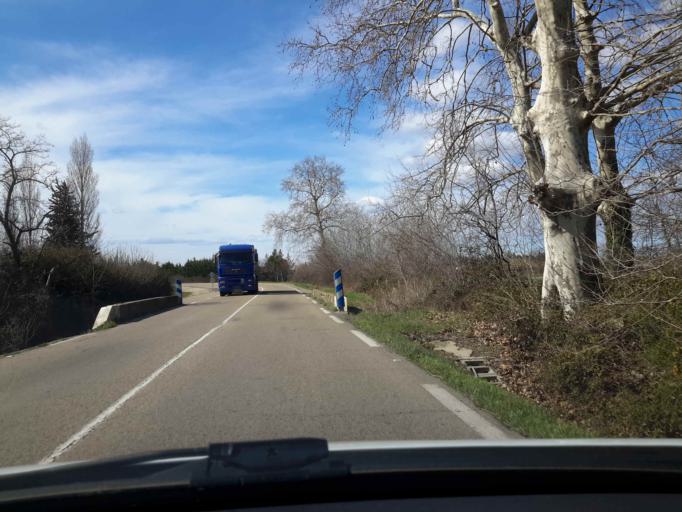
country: FR
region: Languedoc-Roussillon
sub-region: Departement du Gard
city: Le Cailar
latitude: 43.6887
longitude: 4.2431
